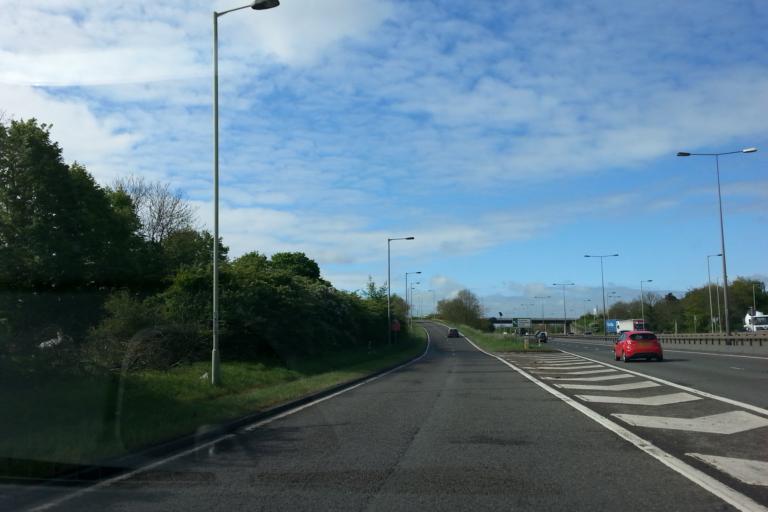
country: GB
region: England
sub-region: Staffordshire
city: Alrewas
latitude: 52.7283
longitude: -1.7438
